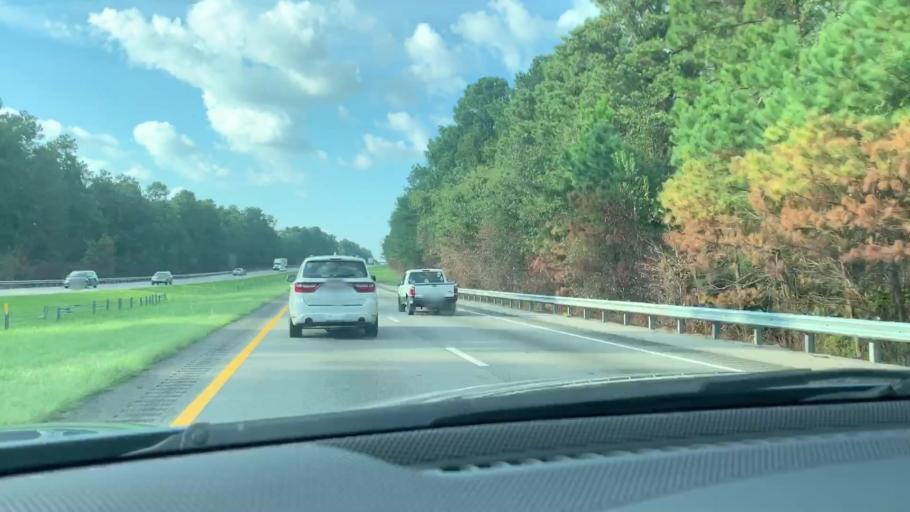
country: US
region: South Carolina
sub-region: Calhoun County
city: Oak Grove
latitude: 33.6906
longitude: -80.9101
